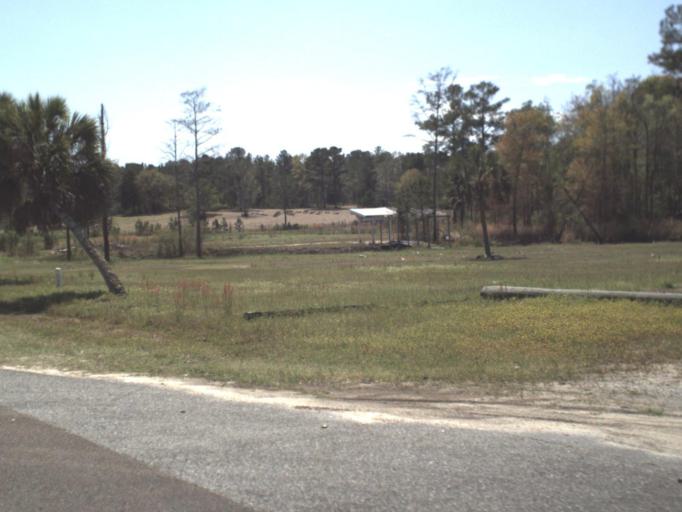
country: US
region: Florida
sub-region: Walton County
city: DeFuniak Springs
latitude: 30.7068
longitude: -85.9336
